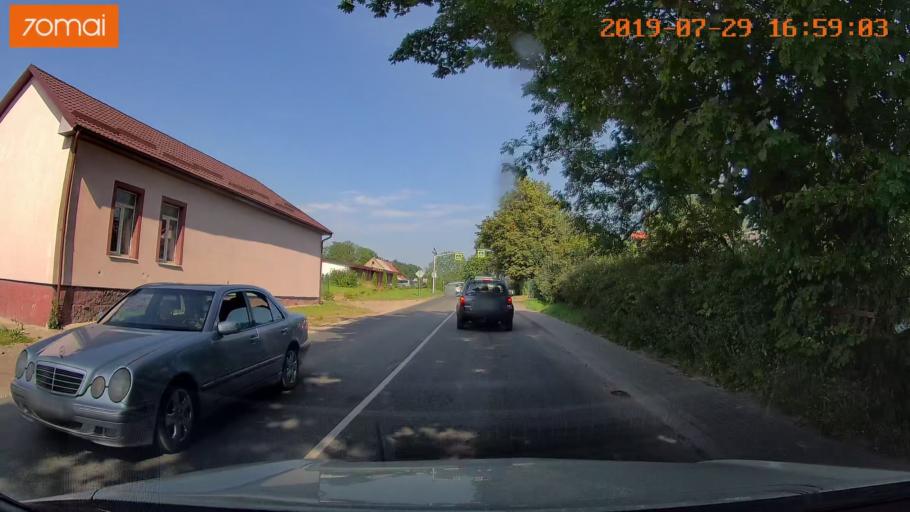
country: RU
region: Kaliningrad
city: Volochayevskoye
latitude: 54.8194
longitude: 20.2109
